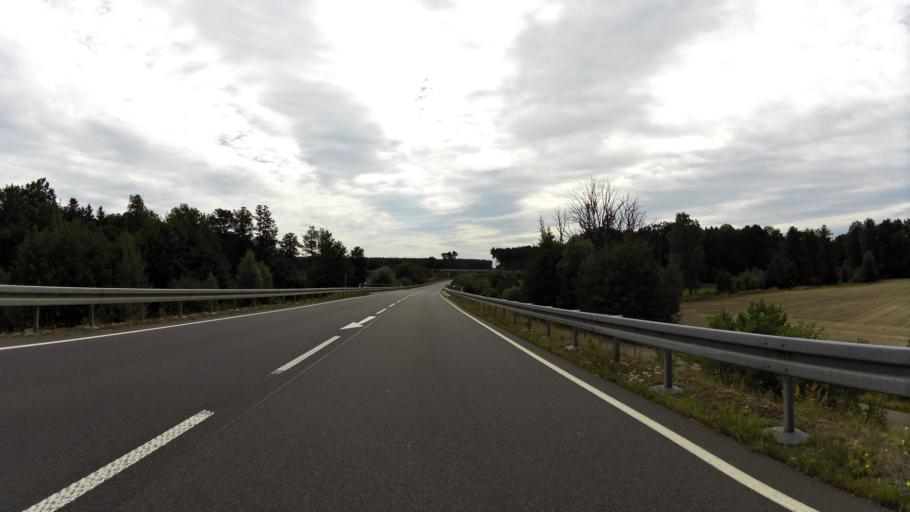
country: DE
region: Brandenburg
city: Schenkendobern
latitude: 51.9654
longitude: 14.6485
